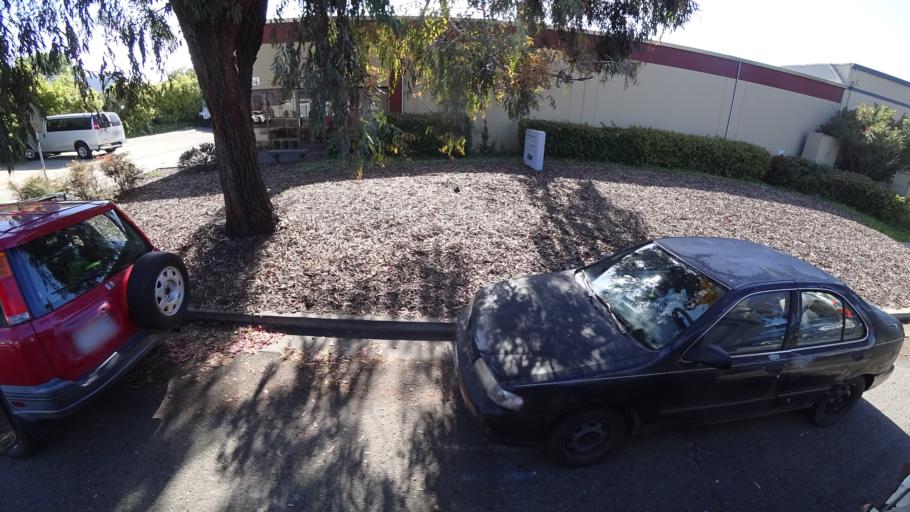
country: US
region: California
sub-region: Alameda County
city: San Lorenzo
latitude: 37.6432
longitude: -122.1331
